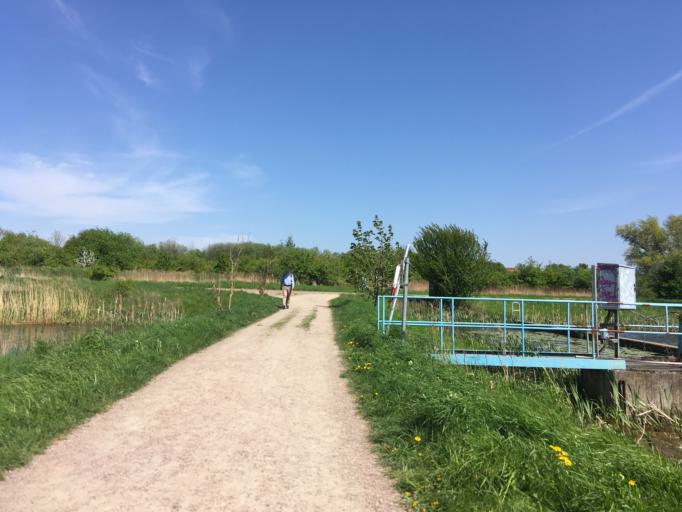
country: SE
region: Skane
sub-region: Staffanstorps Kommun
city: Hjaerup
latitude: 55.7011
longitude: 13.1483
